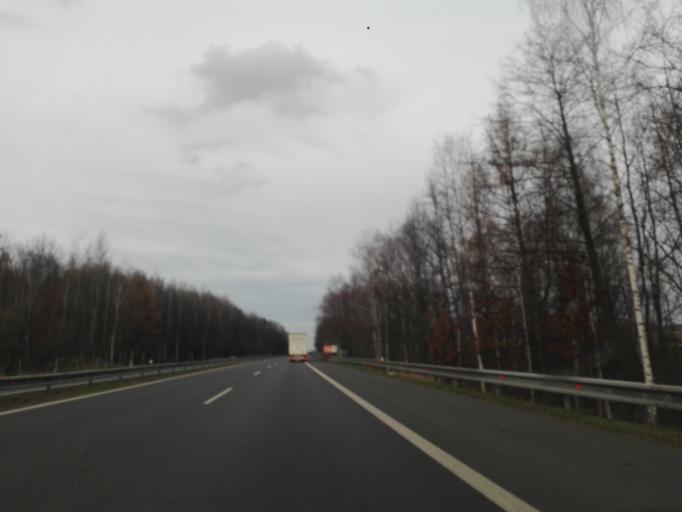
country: CZ
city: Paskov
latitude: 49.7159
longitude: 18.2829
